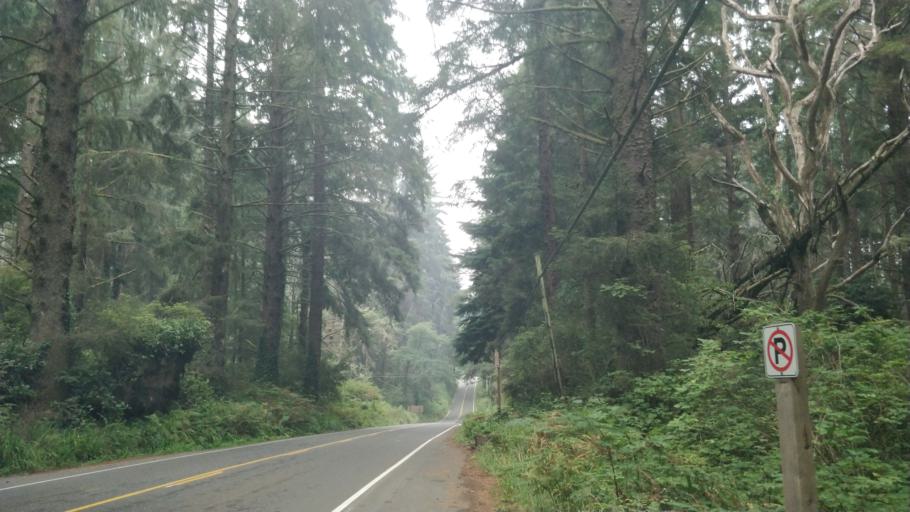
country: US
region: California
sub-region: Humboldt County
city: Westhaven-Moonstone
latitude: 41.1332
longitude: -124.1532
